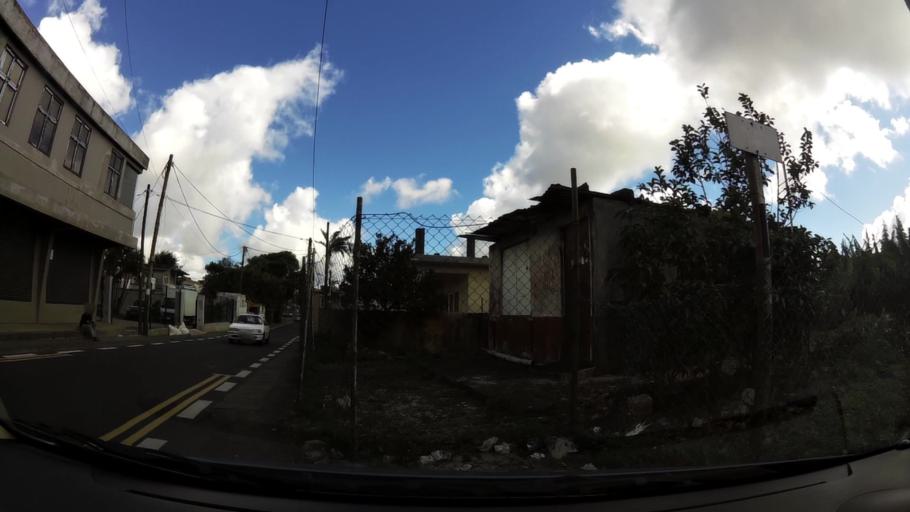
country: MU
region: Plaines Wilhems
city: Curepipe
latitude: -20.3297
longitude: 57.5263
